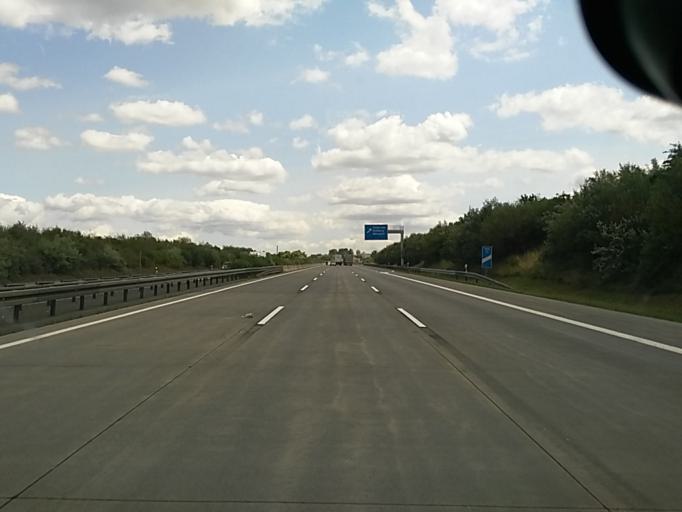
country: DE
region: Thuringia
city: Quirla
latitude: 50.8670
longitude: 11.7688
